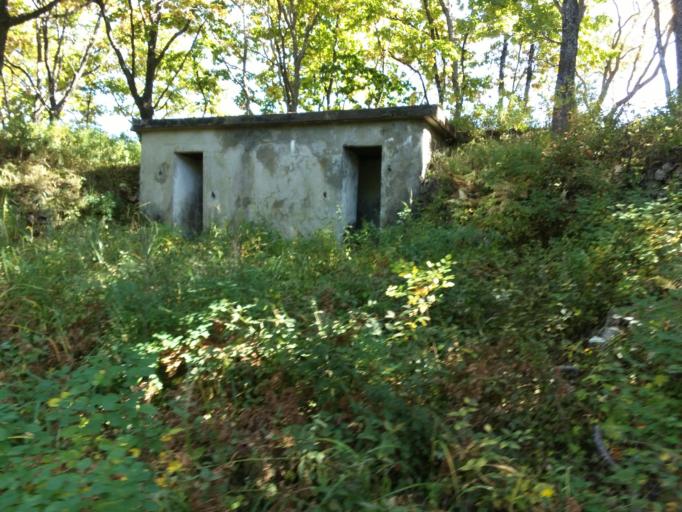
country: RU
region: Primorskiy
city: Zarubino
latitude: 42.6906
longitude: 131.2388
